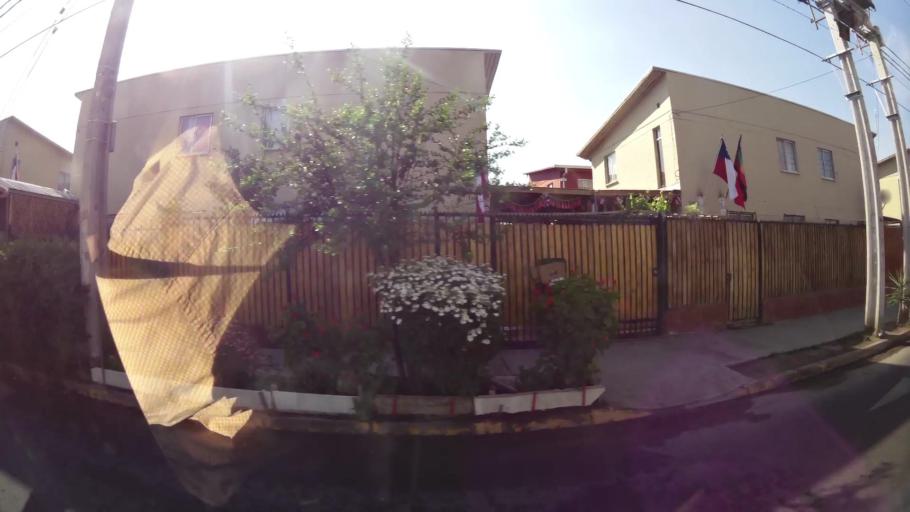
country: CL
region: Santiago Metropolitan
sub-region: Provincia de Santiago
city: Lo Prado
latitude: -33.4212
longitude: -70.7600
